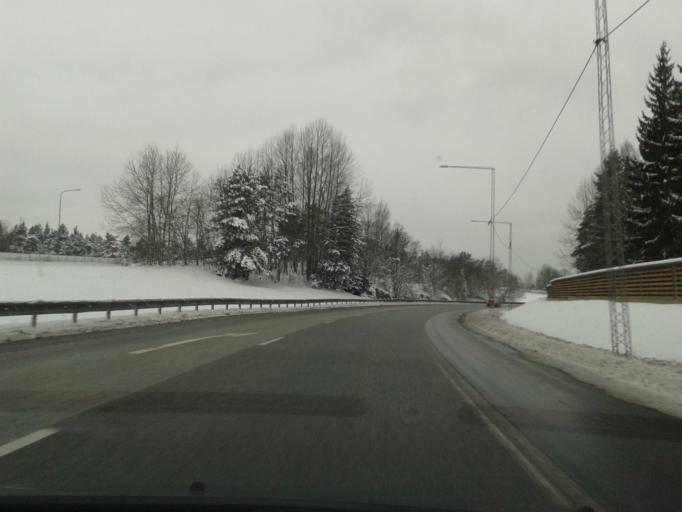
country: SE
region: Stockholm
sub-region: Nacka Kommun
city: Alta
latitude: 59.2454
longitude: 18.1839
